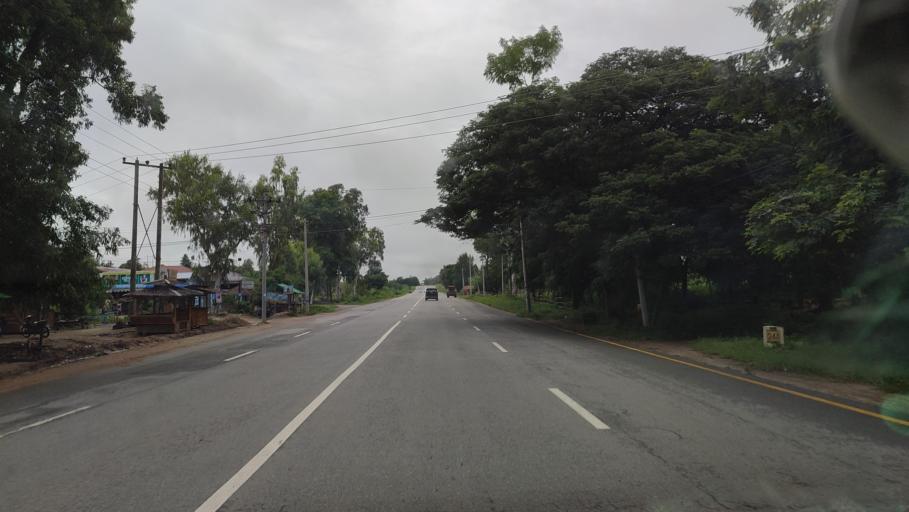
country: MM
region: Mandalay
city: Pyinmana
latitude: 19.9967
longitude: 96.2476
